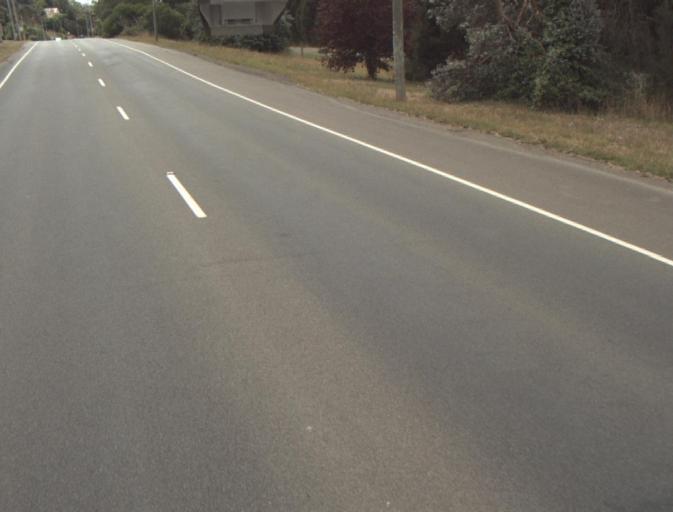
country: AU
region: Tasmania
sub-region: Launceston
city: Launceston
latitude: -41.4348
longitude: 147.1241
